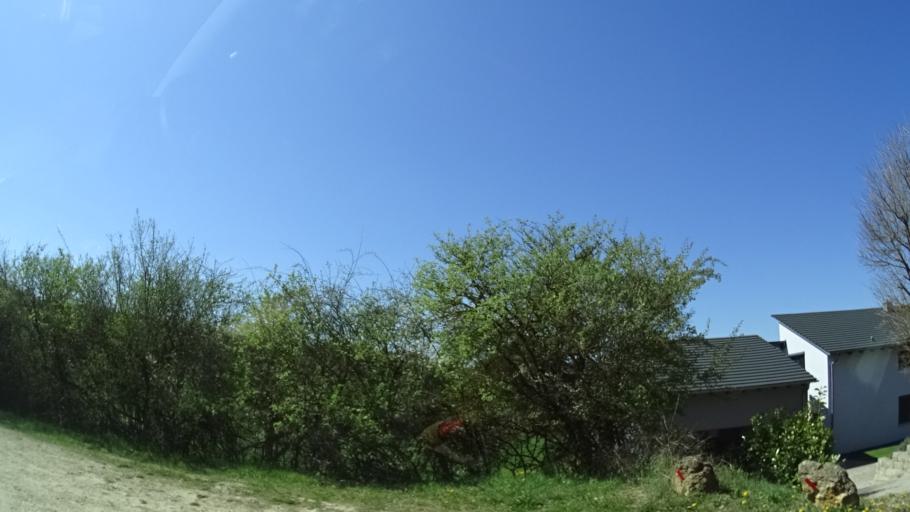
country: DE
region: Bavaria
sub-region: Upper Palatinate
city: Illschwang
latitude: 49.4114
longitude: 11.6439
